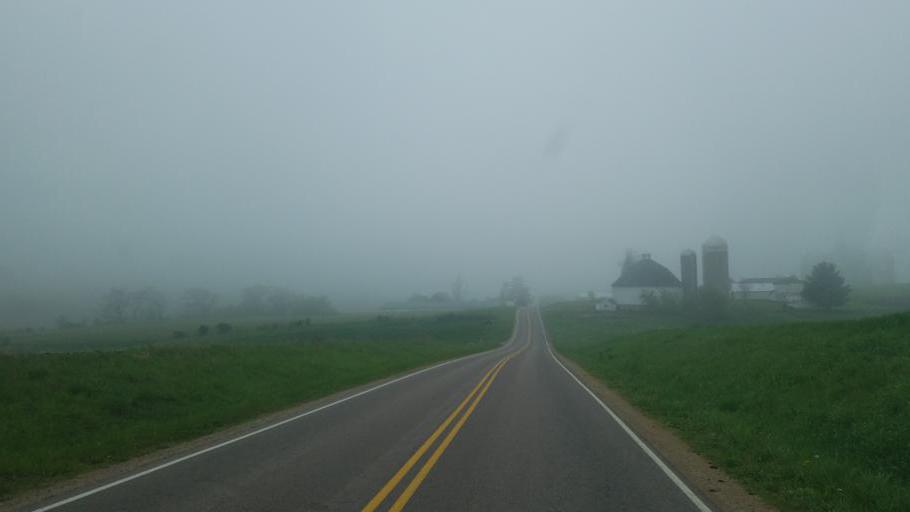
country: US
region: Wisconsin
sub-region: Vernon County
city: Hillsboro
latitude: 43.6434
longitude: -90.3525
